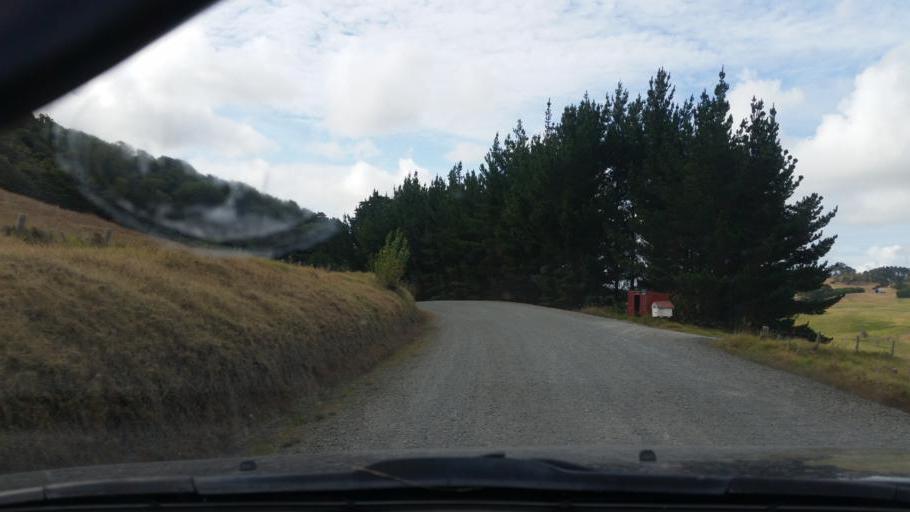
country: NZ
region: Northland
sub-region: Kaipara District
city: Dargaville
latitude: -35.9778
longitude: 173.9531
